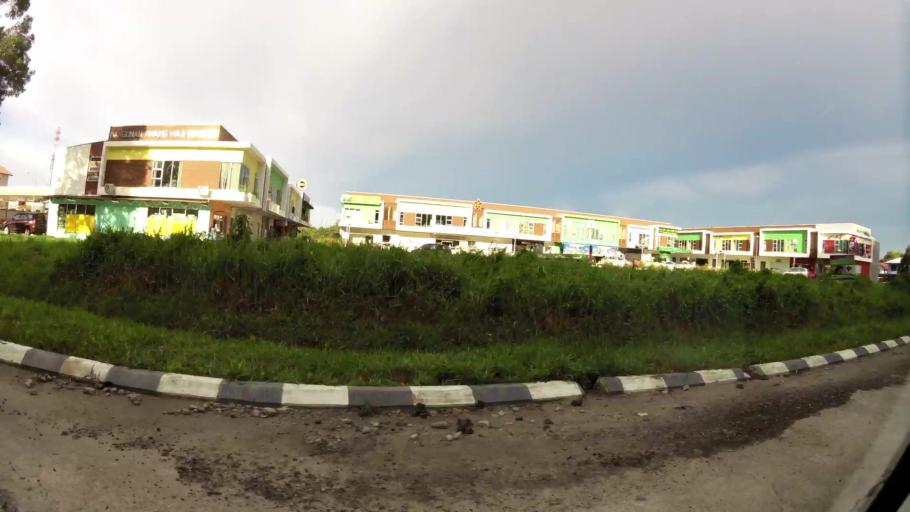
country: BN
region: Brunei and Muara
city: Bandar Seri Begawan
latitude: 4.9558
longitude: 115.0203
